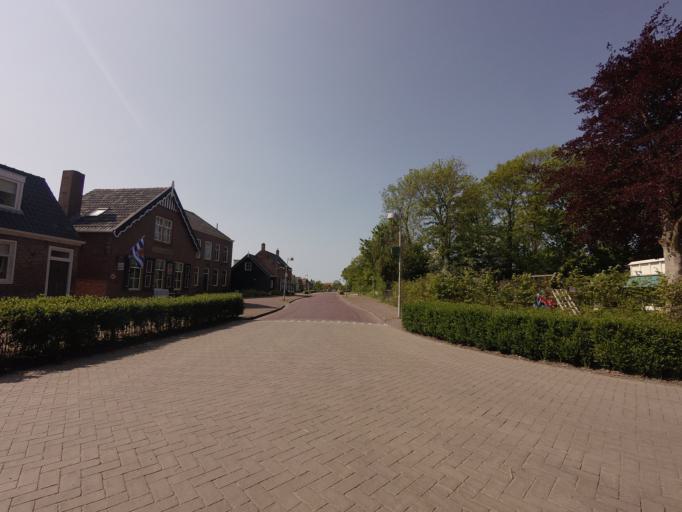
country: NL
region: Zeeland
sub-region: Gemeente Middelburg
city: Middelburg
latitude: 51.5490
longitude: 3.5915
